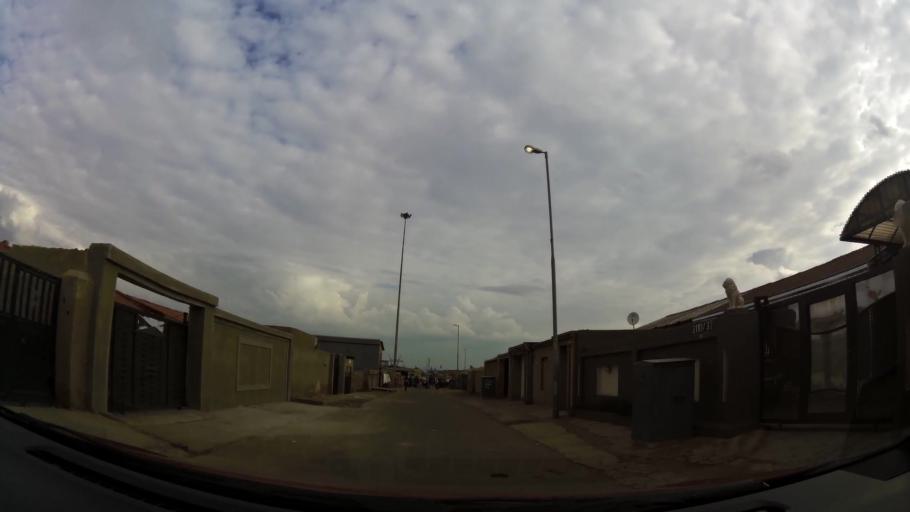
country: ZA
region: Gauteng
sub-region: City of Johannesburg Metropolitan Municipality
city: Soweto
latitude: -26.2451
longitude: 27.8391
